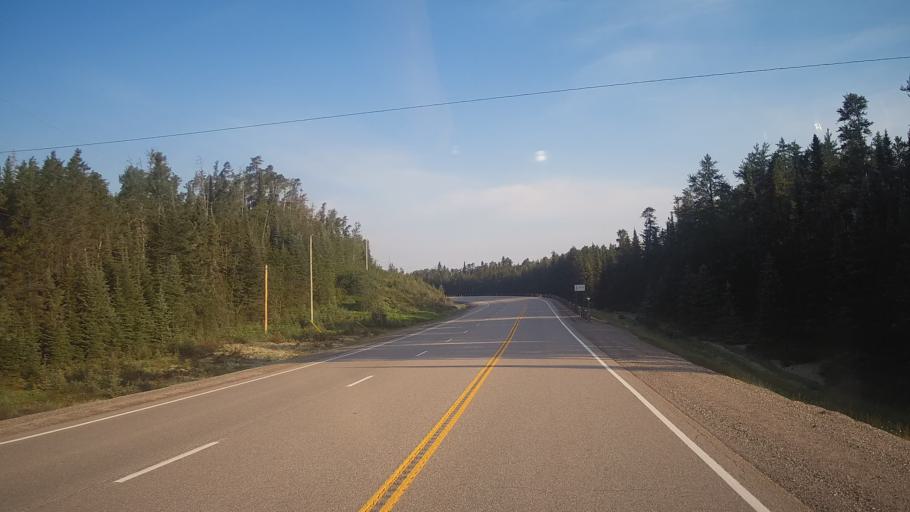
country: CA
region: Ontario
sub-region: Rainy River District
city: Atikokan
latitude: 49.3416
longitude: -91.4770
